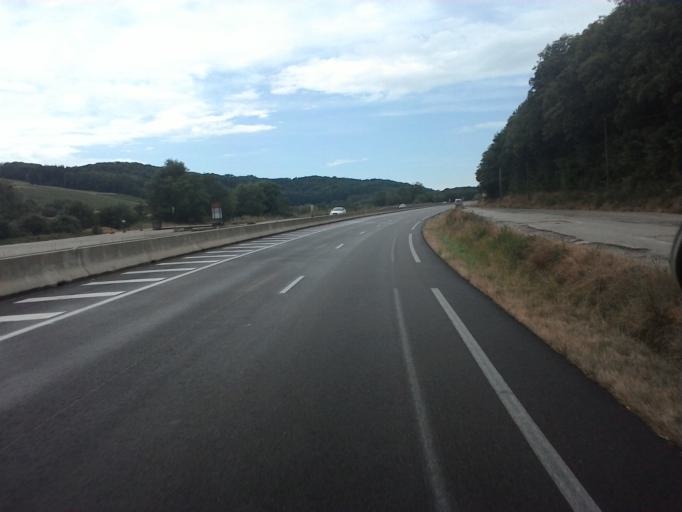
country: FR
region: Franche-Comte
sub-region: Departement du Jura
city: Poligny
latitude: 46.8041
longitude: 5.5774
